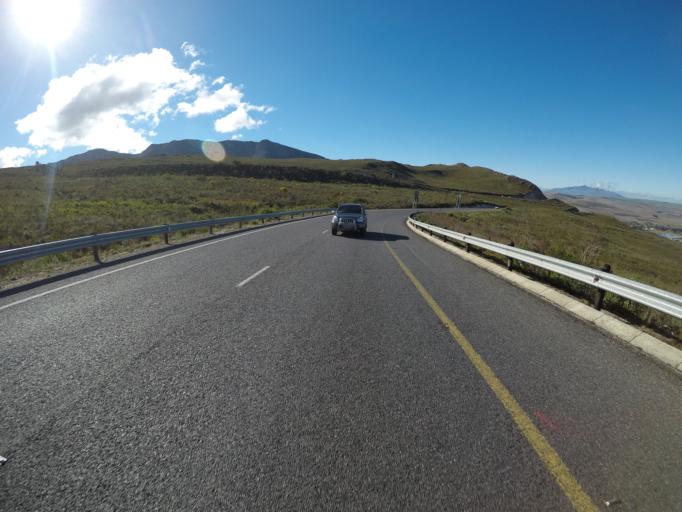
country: ZA
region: Western Cape
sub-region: Overberg District Municipality
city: Grabouw
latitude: -34.2230
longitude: 19.1749
